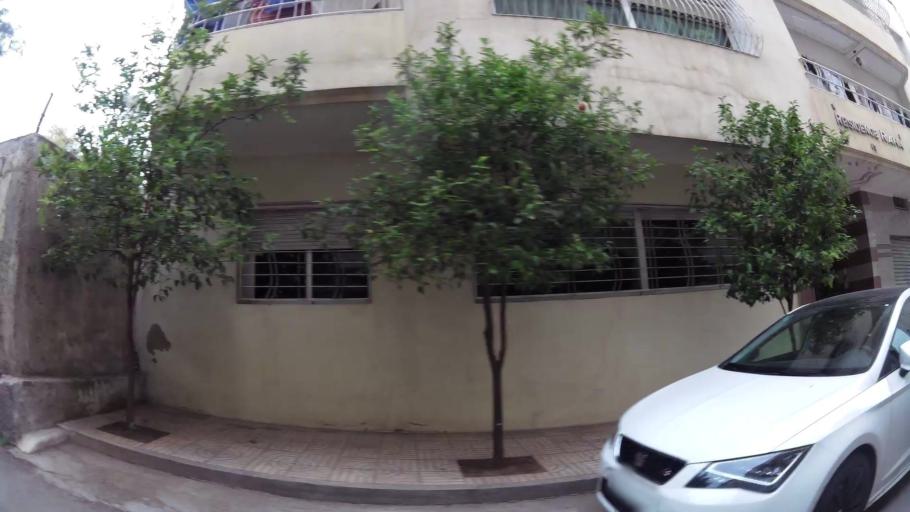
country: MA
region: Fes-Boulemane
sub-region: Fes
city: Fes
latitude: 34.0289
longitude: -4.9958
